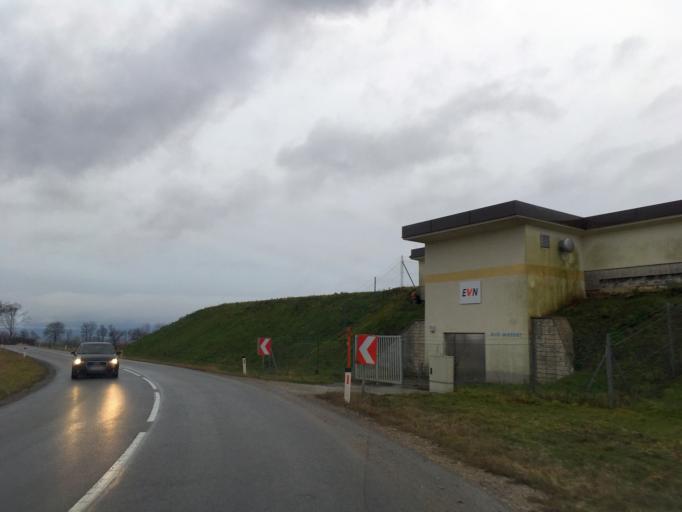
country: AT
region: Lower Austria
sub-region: Politischer Bezirk Wien-Umgebung
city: Rauchenwarth
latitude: 48.0693
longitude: 16.5325
